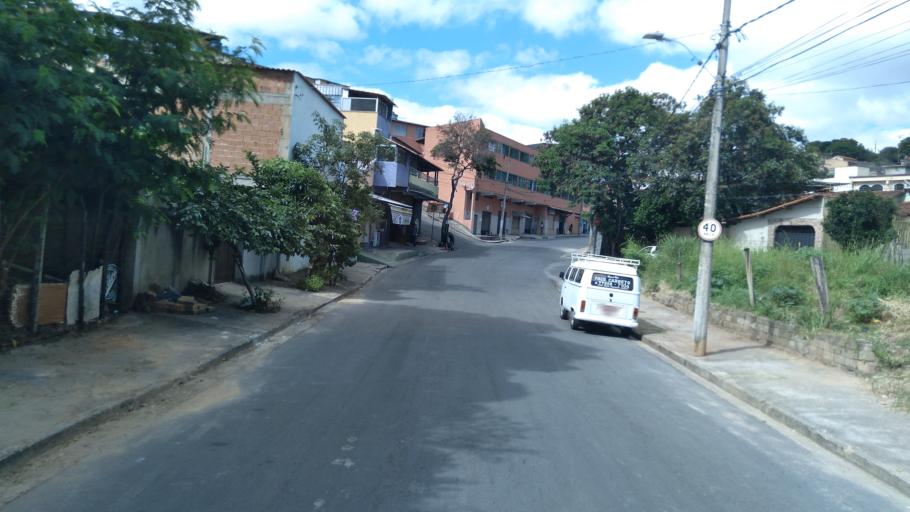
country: BR
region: Minas Gerais
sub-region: Belo Horizonte
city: Belo Horizonte
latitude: -19.8632
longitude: -43.9109
